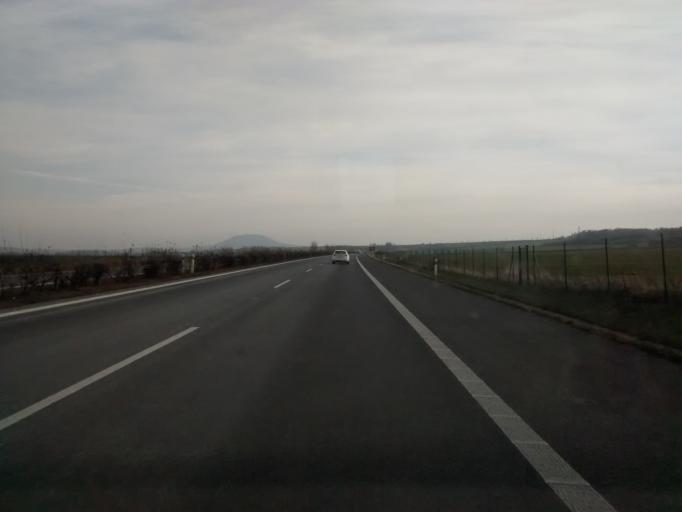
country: CZ
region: Ustecky
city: Roudnice nad Labem
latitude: 50.4305
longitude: 14.1946
